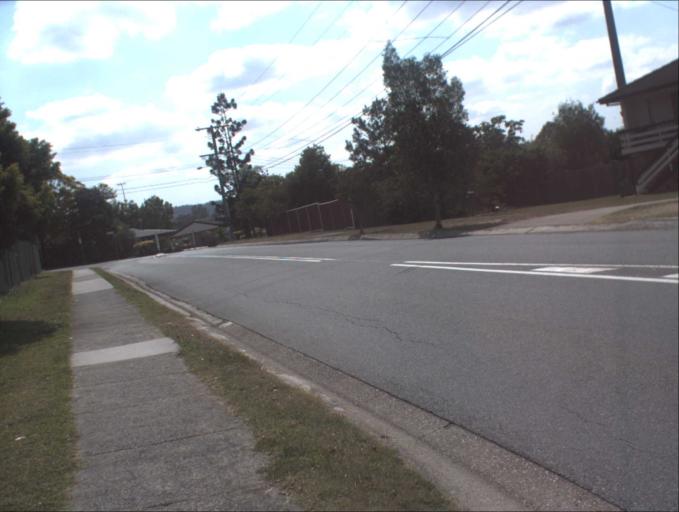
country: AU
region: Queensland
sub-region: Logan
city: Slacks Creek
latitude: -27.6445
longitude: 153.1556
